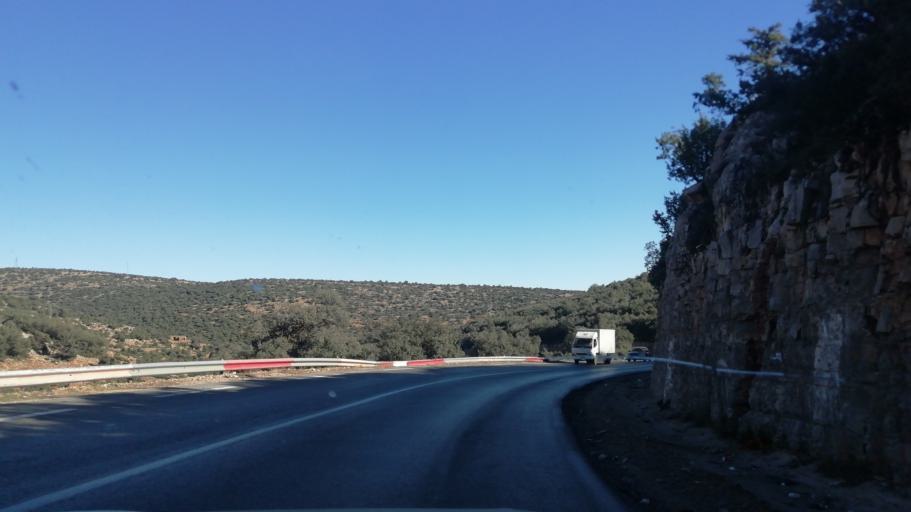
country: DZ
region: Tlemcen
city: Sebdou
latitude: 34.7401
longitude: -1.3442
